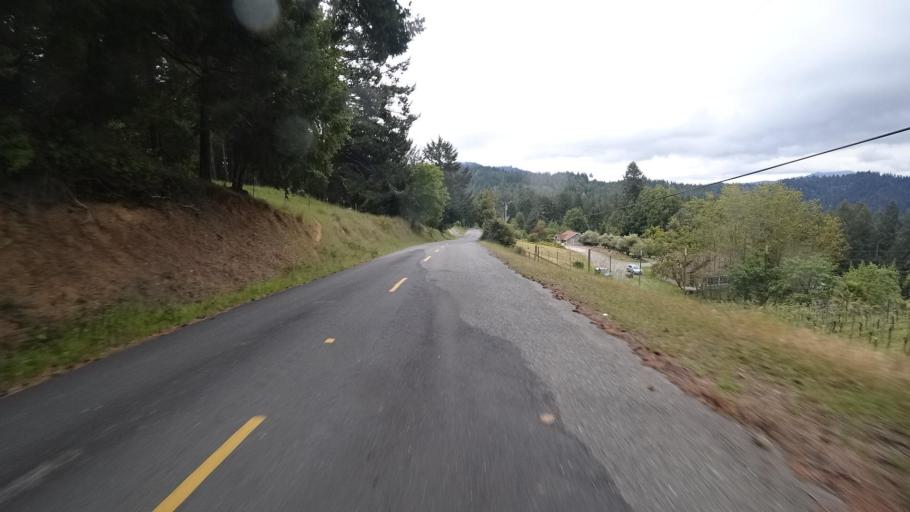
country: US
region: California
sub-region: Humboldt County
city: Redway
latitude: 40.2868
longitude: -123.8010
